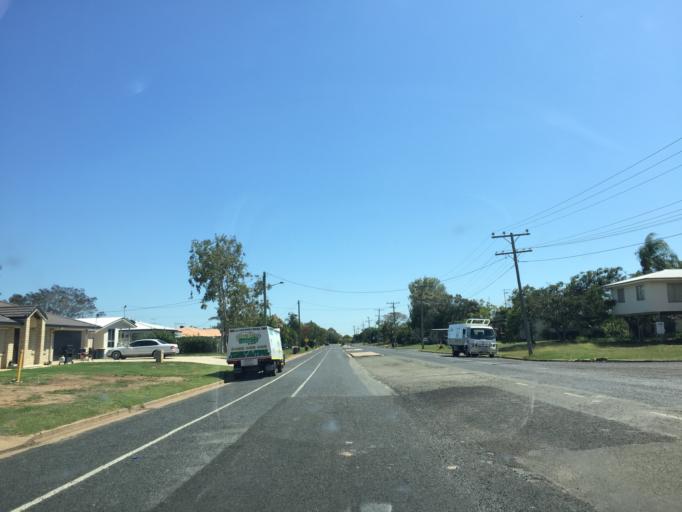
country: AU
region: Queensland
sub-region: Central Highlands
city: Blackwater
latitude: -23.5851
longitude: 148.8724
